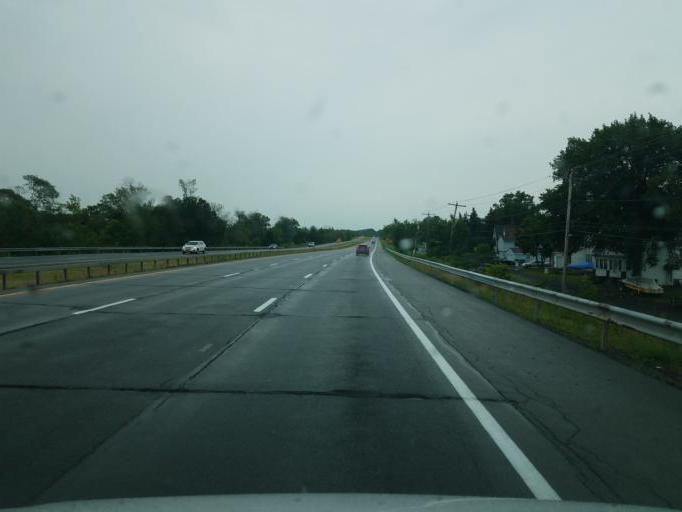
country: US
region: New York
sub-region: Erie County
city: Grandyle Village
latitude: 43.0779
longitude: -78.9571
